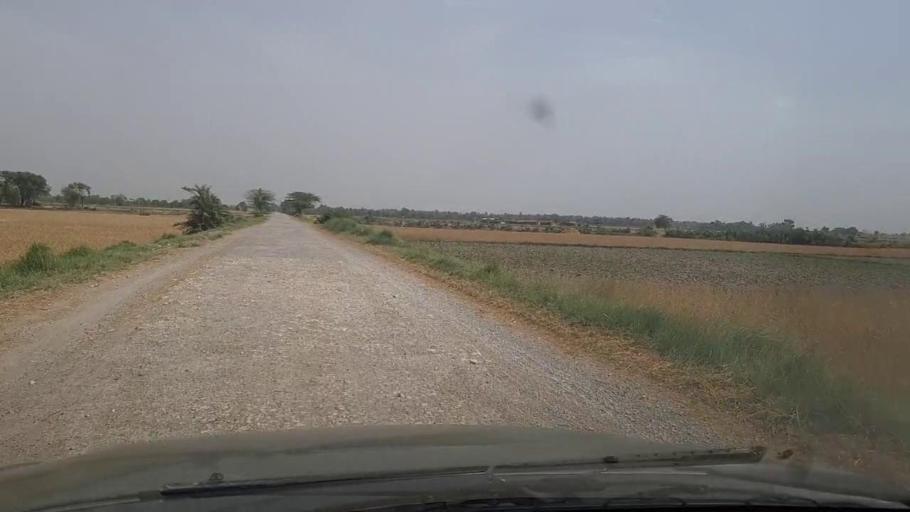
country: PK
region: Sindh
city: Lakhi
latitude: 27.8499
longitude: 68.7528
